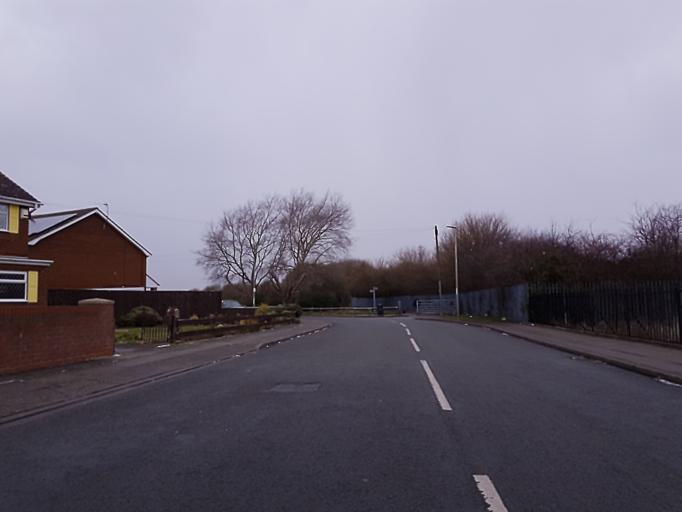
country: GB
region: England
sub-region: North East Lincolnshire
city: Grimbsy
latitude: 53.5639
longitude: -0.1171
